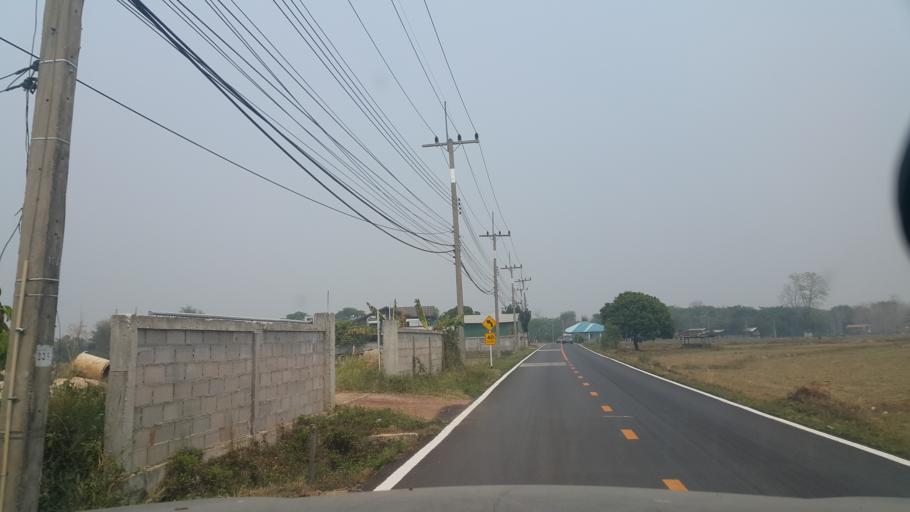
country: TH
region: Lampang
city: Hang Chat
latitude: 18.2561
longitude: 99.2471
